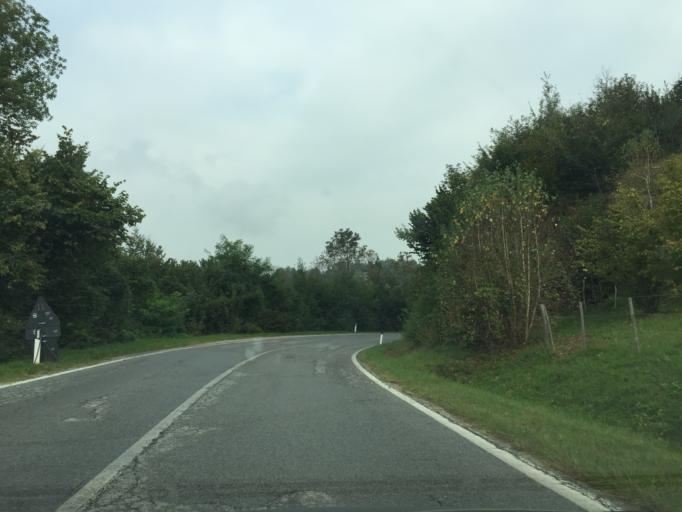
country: IT
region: Piedmont
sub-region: Provincia di Cuneo
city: Roccaforte Mondovi
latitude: 44.3107
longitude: 7.7089
